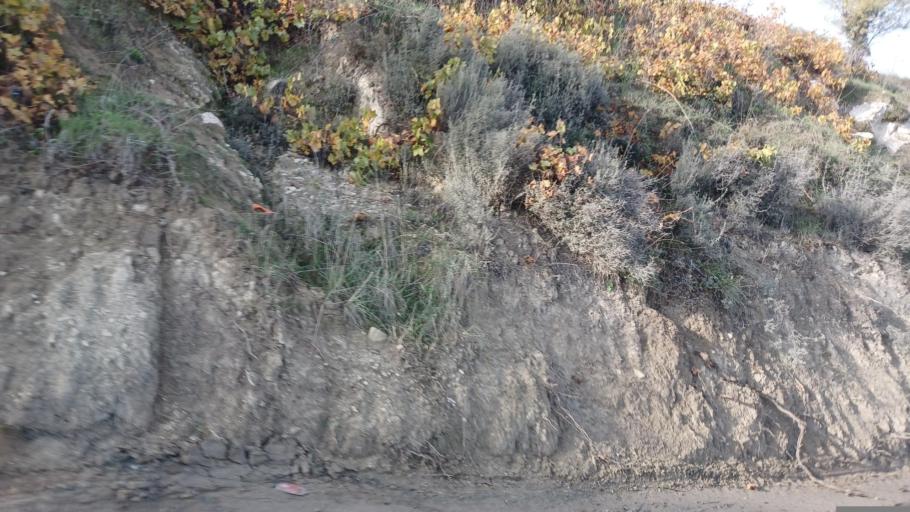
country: CY
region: Pafos
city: Tala
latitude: 34.9068
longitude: 32.4695
